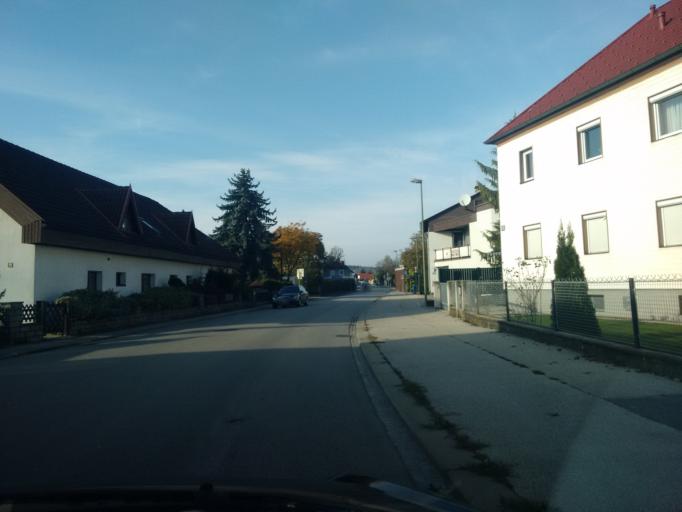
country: AT
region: Upper Austria
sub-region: Wels Stadt
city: Wels
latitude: 48.1726
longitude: 14.0053
